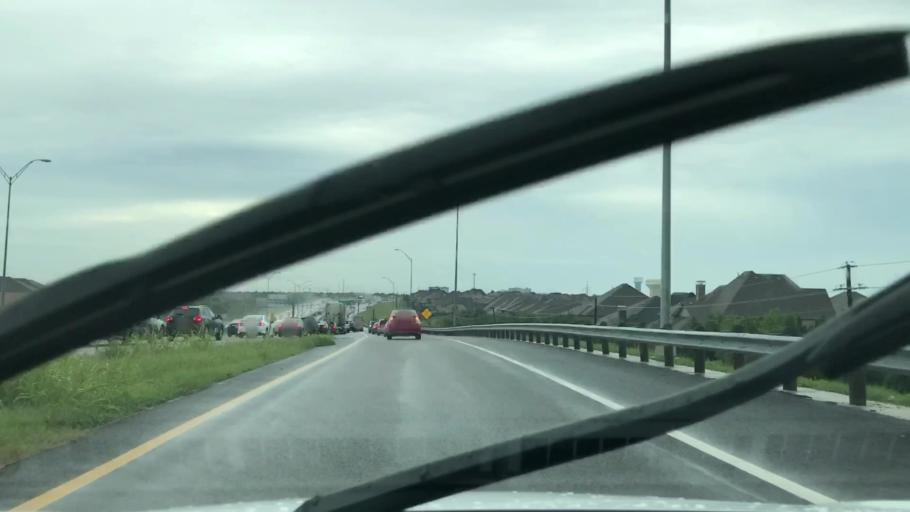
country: US
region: Texas
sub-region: Dallas County
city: Coppell
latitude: 32.9009
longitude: -96.9811
